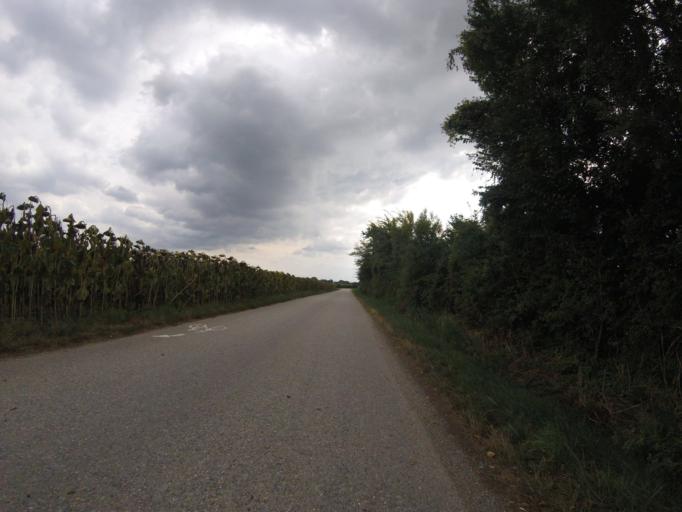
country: AT
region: Burgenland
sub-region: Eisenstadt-Umgebung
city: Donnerskirchen
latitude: 47.9027
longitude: 16.6720
